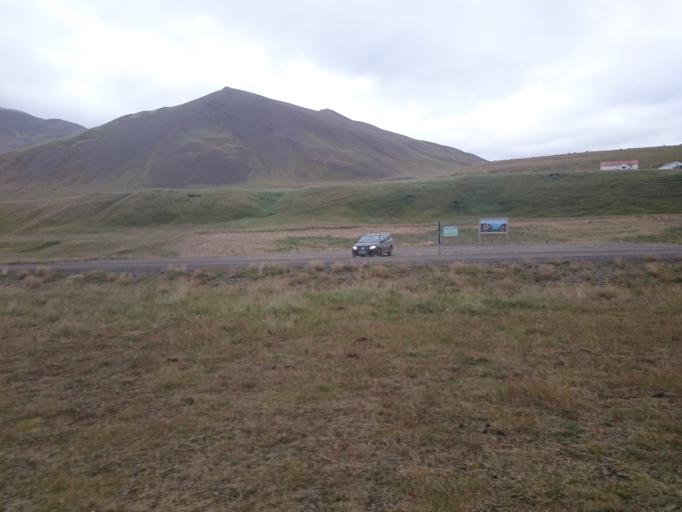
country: IS
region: Westfjords
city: Isafjoerdur
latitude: 65.7572
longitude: -23.4594
